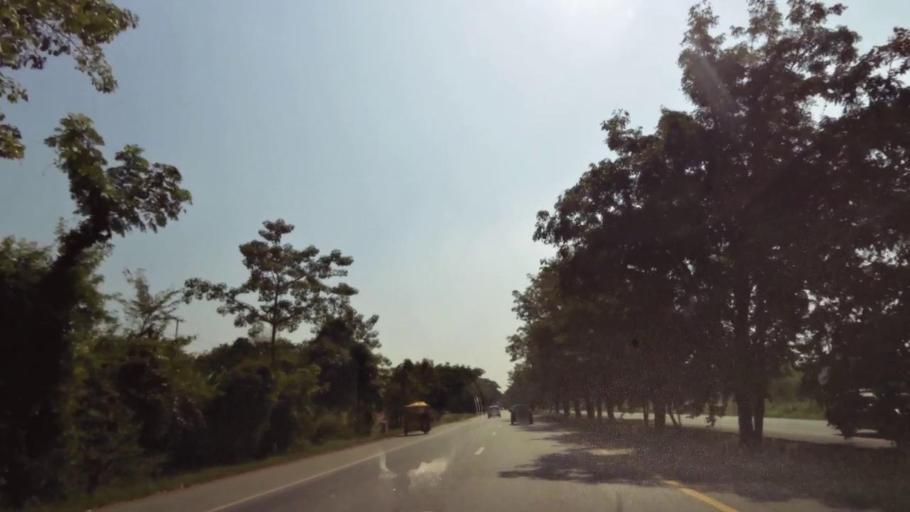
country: TH
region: Phichit
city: Bueng Na Rang
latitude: 16.0195
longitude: 100.1145
